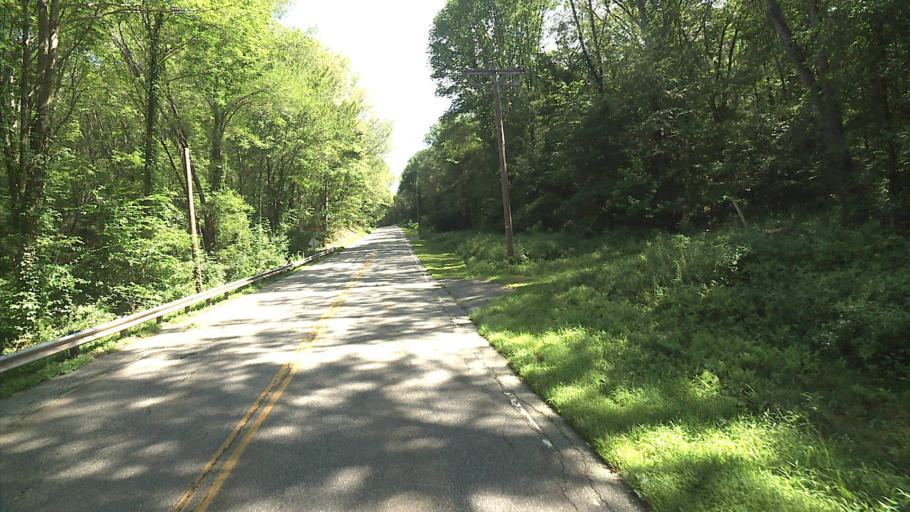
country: US
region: Connecticut
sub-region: New London County
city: Baltic
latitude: 41.6579
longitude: -72.0918
